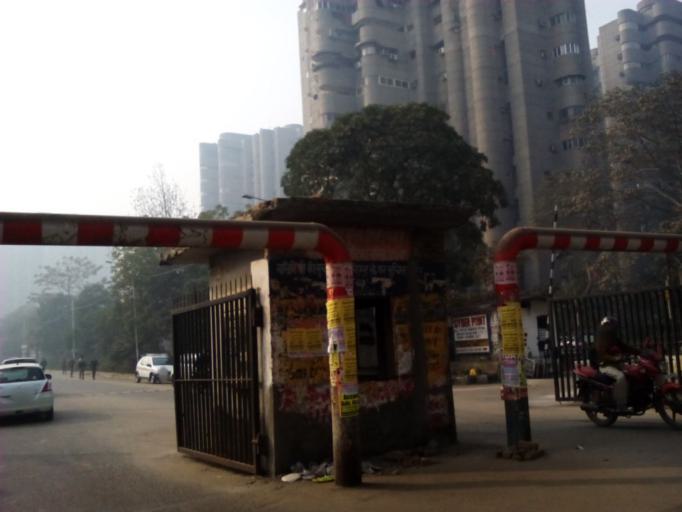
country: IN
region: Uttar Pradesh
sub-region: Gautam Buddha Nagar
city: Noida
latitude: 28.6452
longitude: 77.3203
